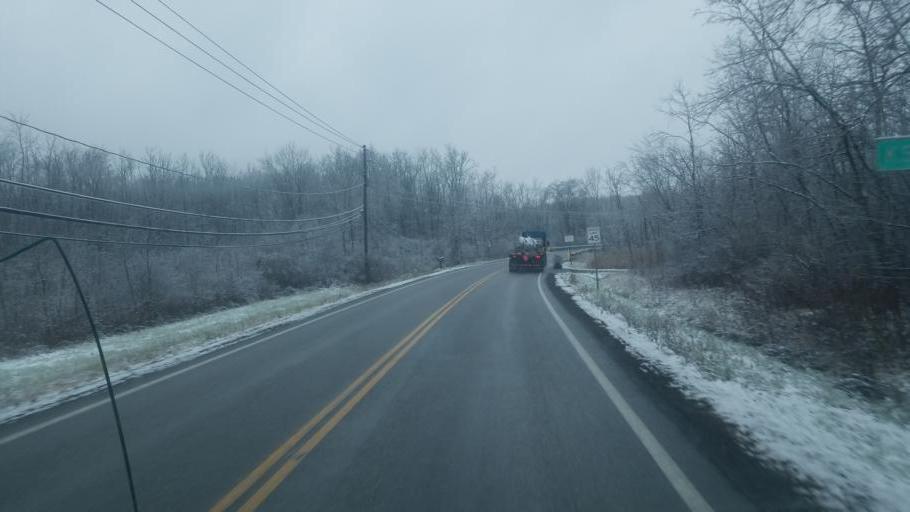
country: US
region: Ohio
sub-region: Geauga County
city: Burton
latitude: 41.4584
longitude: -81.1364
